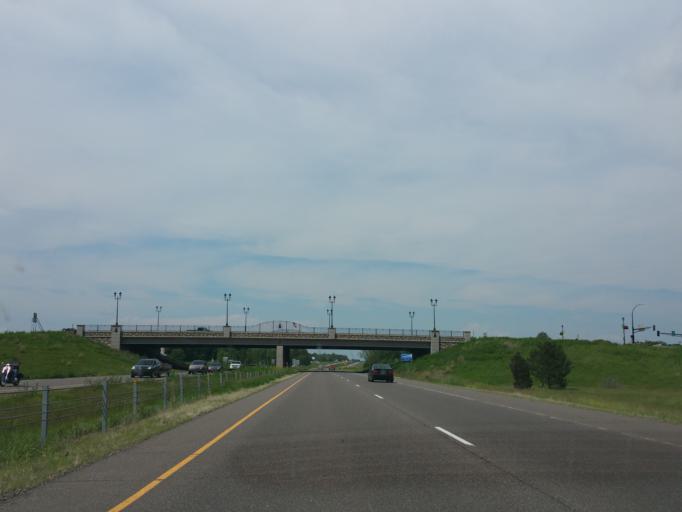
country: US
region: Minnesota
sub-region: Chisago County
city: North Branch
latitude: 45.5086
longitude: -92.9931
